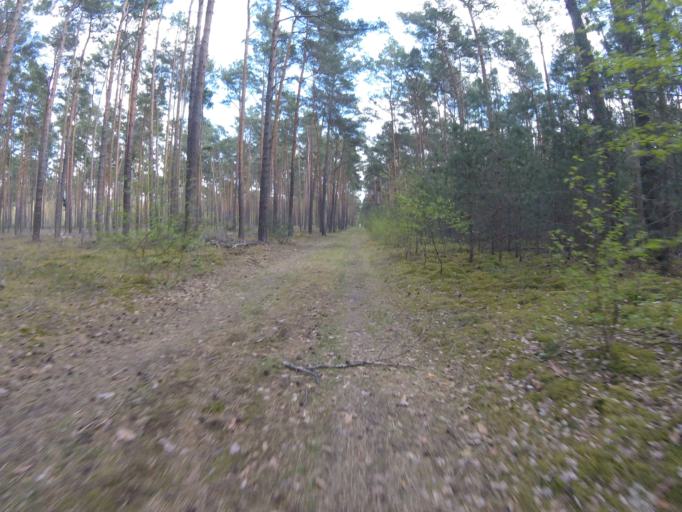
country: DE
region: Brandenburg
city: Gross Koris
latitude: 52.1883
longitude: 13.7208
